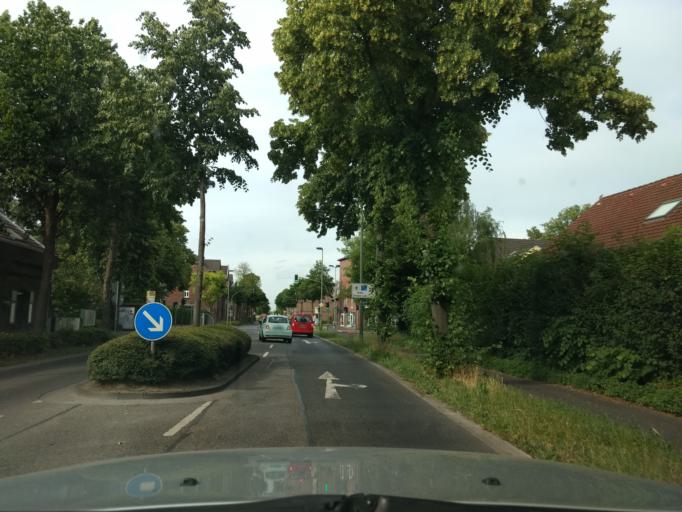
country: DE
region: North Rhine-Westphalia
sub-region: Regierungsbezirk Dusseldorf
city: Meerbusch
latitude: 51.3039
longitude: 6.6720
